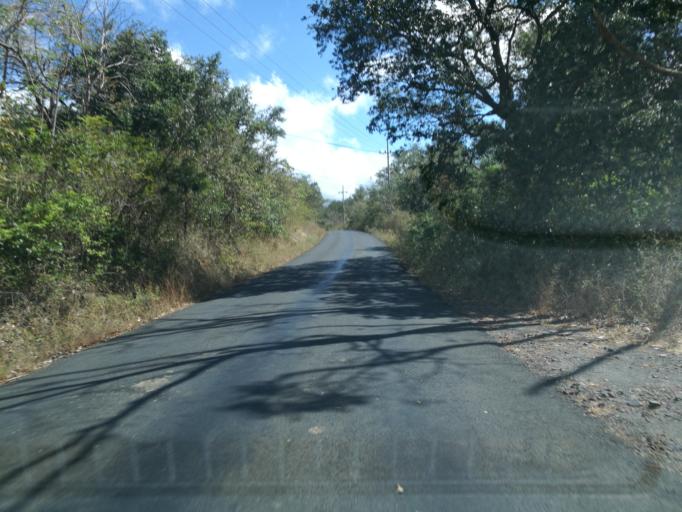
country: CR
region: Guanacaste
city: Liberia
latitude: 10.7419
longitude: -85.3858
